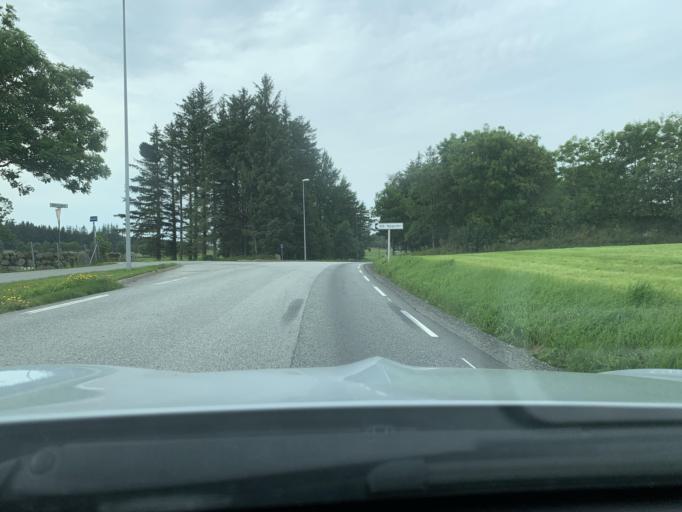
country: NO
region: Rogaland
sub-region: Time
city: Bryne
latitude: 58.7560
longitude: 5.7073
